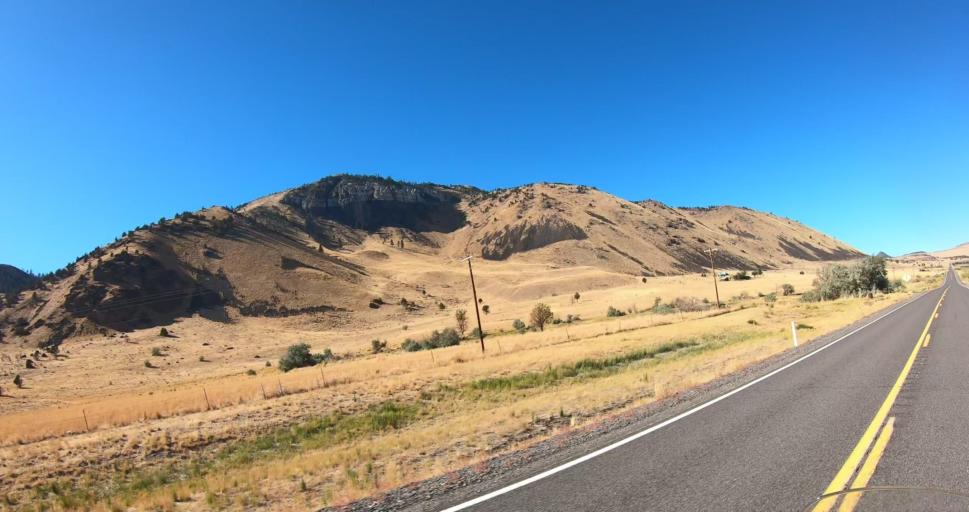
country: US
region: Oregon
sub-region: Lake County
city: Lakeview
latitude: 42.9787
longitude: -120.7777
